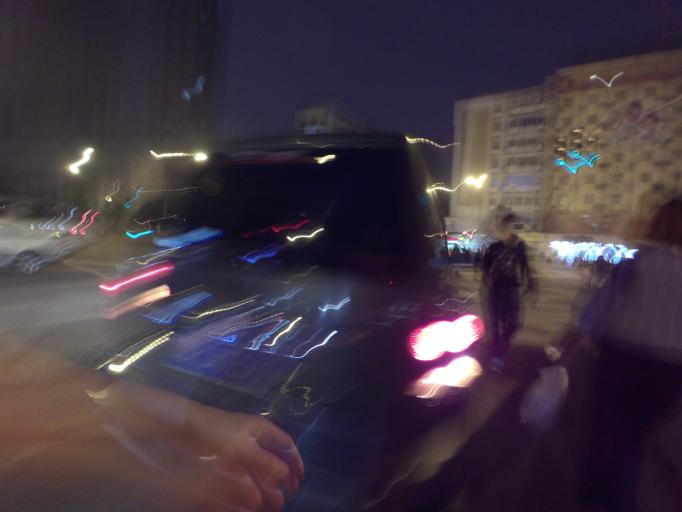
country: CN
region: Sichuan
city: Chengdu
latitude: 30.6692
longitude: 104.0583
